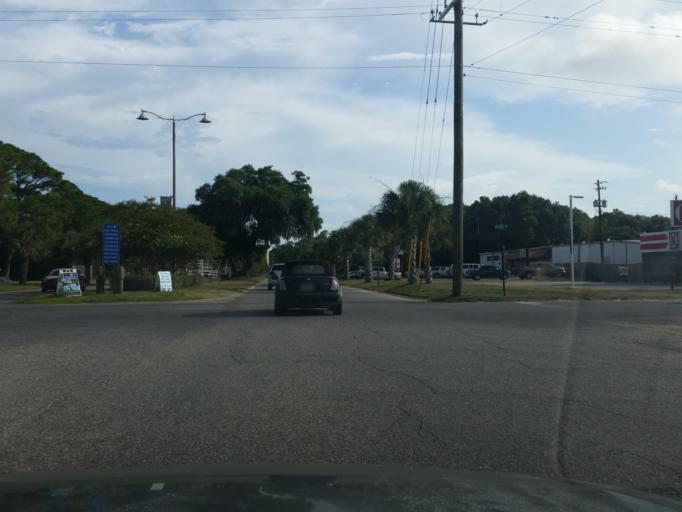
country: US
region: Alabama
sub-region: Mobile County
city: Dauphin Island
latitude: 30.2576
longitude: -88.1126
